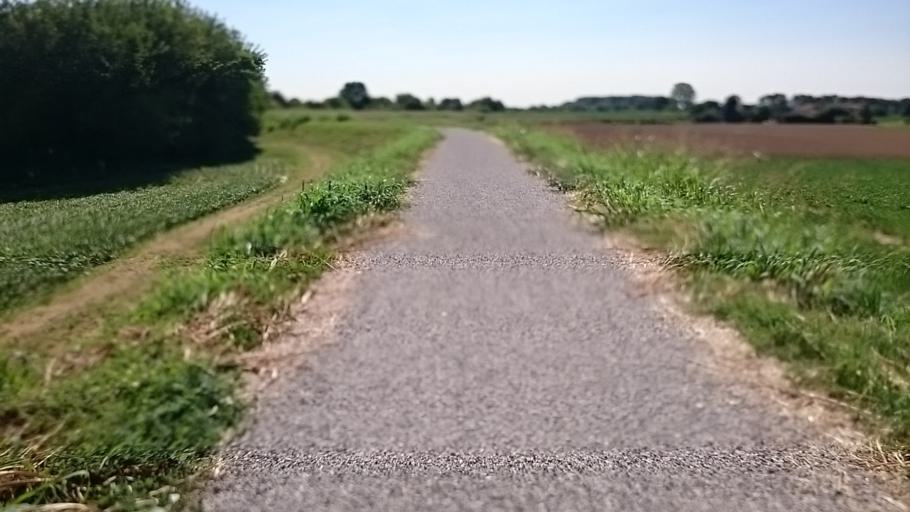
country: IT
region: Veneto
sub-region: Provincia di Padova
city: Cervarese Santa Croce
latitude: 45.4230
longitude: 11.6987
